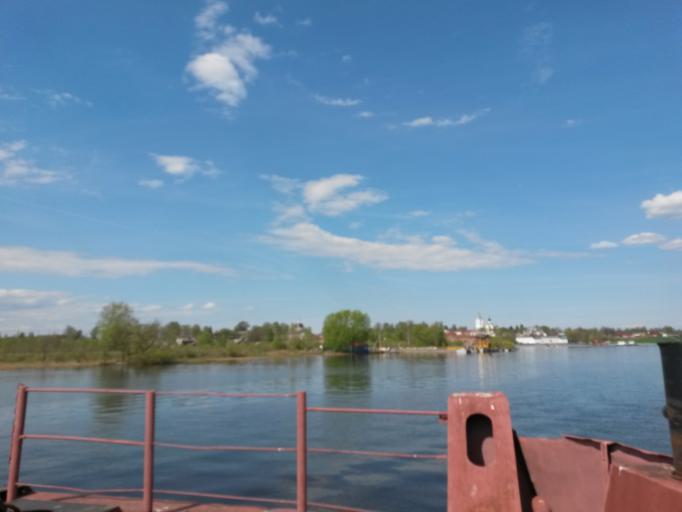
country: RU
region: Jaroslavl
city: Myshkin
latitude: 57.7785
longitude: 38.4543
